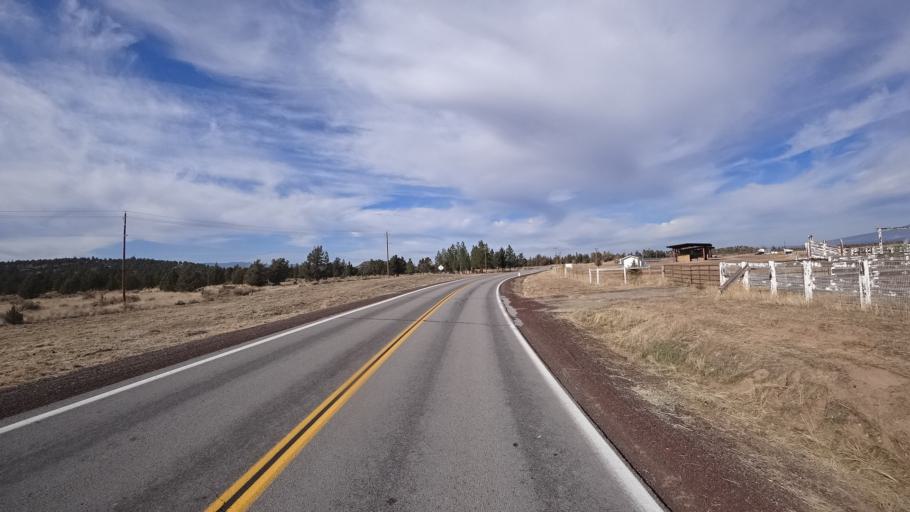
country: US
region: California
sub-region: Siskiyou County
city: Weed
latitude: 41.5502
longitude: -122.3796
